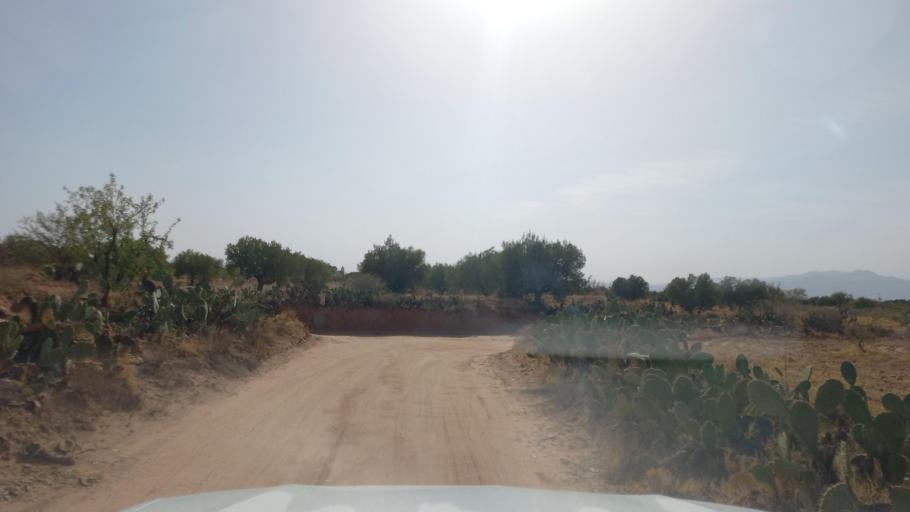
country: TN
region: Al Qasrayn
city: Kasserine
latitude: 35.2051
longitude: 8.9611
